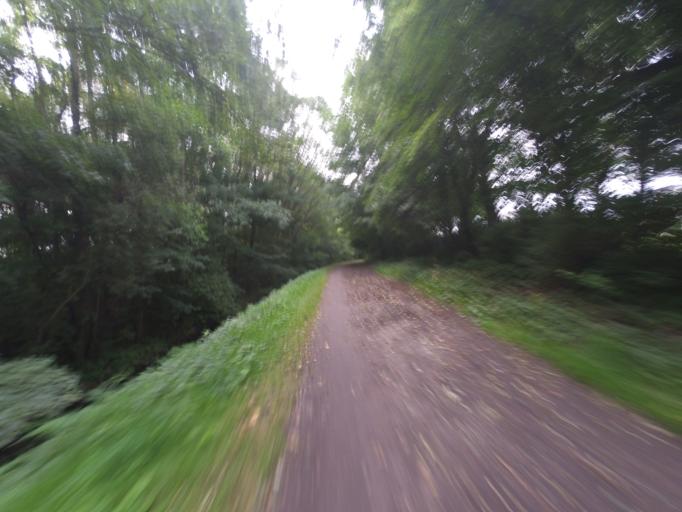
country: DE
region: Hamburg
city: Wandsbek
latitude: 53.5488
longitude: 10.1195
